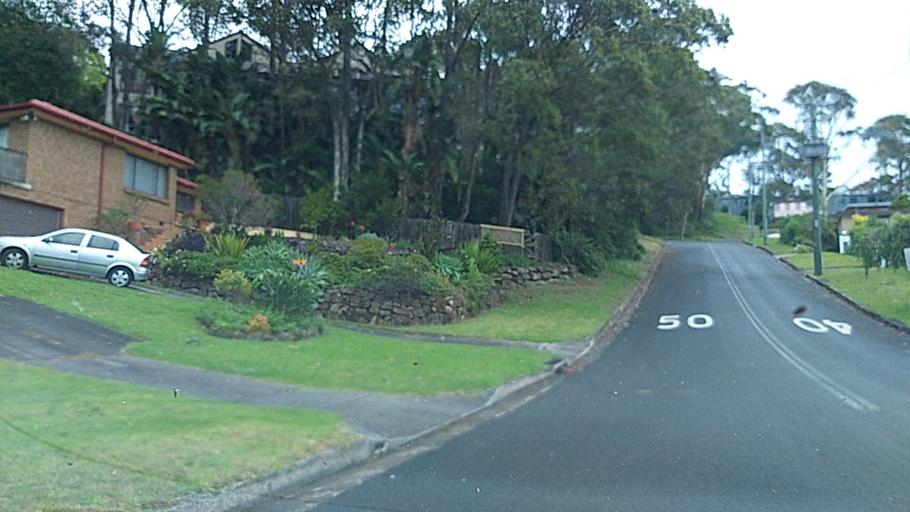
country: AU
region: New South Wales
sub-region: Wollongong
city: Mangerton
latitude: -34.4386
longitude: 150.8768
